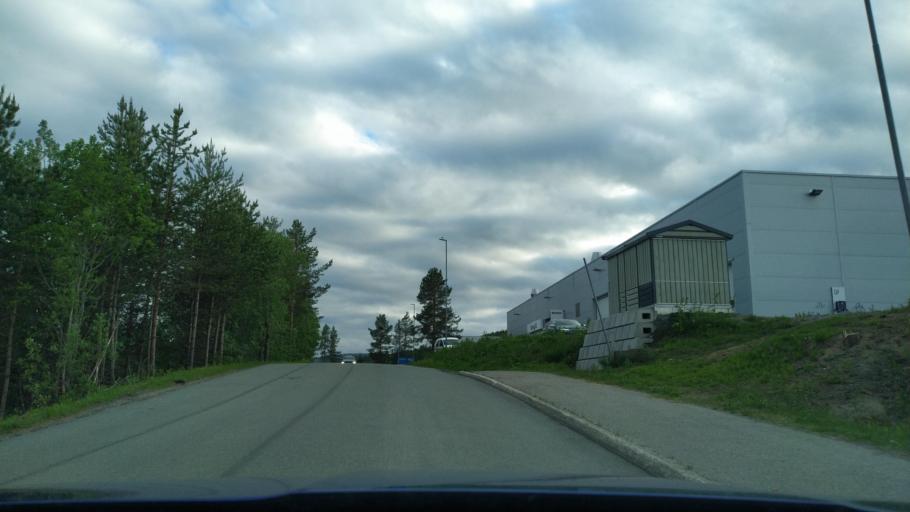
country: NO
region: Troms
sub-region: Malselv
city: Moen
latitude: 69.0923
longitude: 18.5907
